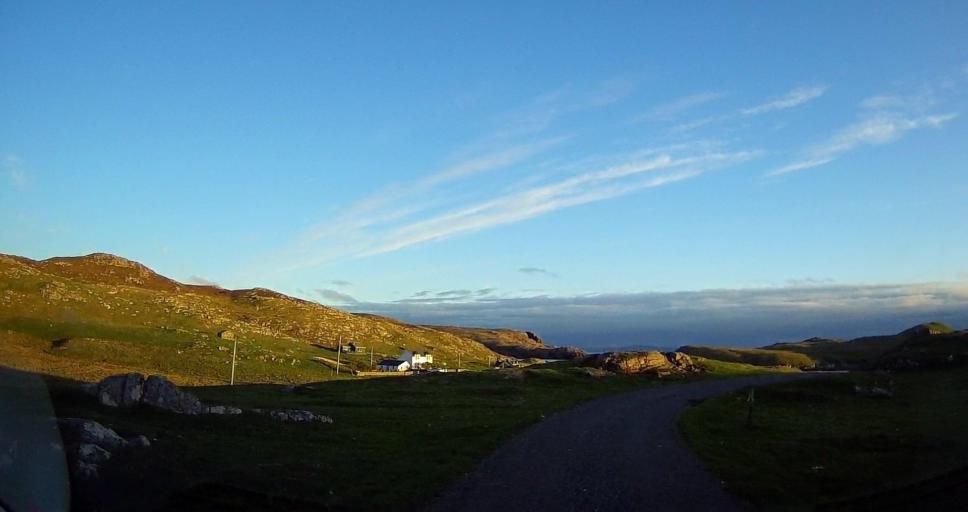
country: GB
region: Scotland
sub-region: Shetland Islands
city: Lerwick
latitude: 60.4427
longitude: -1.4466
